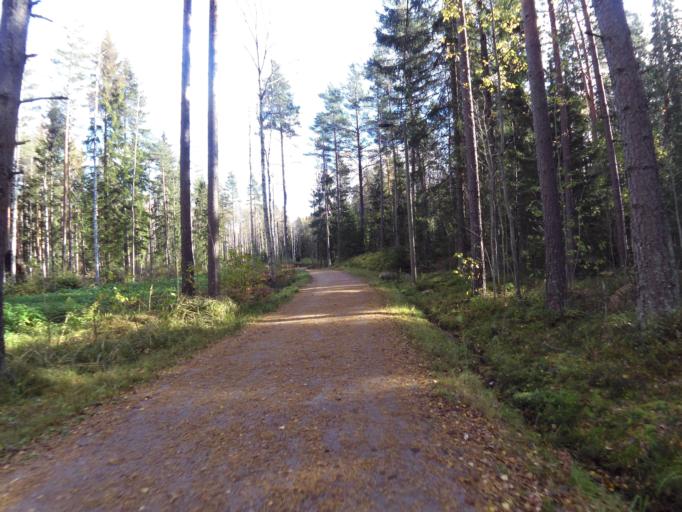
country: FI
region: Uusimaa
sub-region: Helsinki
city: Espoo
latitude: 60.1806
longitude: 24.6365
